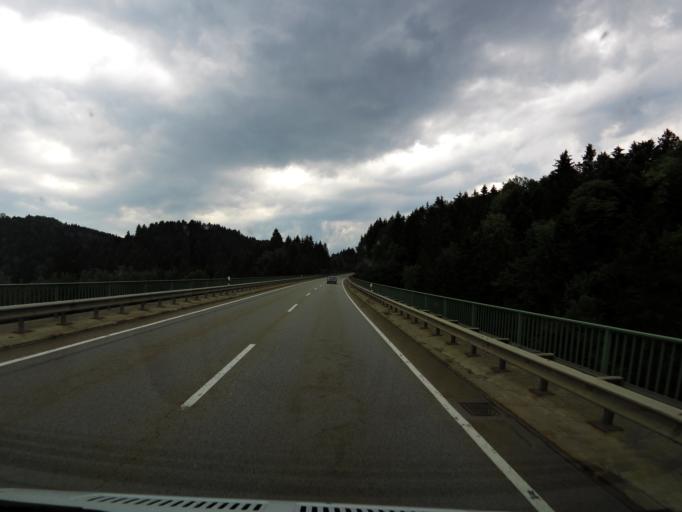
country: DE
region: Bavaria
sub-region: Lower Bavaria
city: Hutthurm
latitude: 48.6853
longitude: 13.4453
